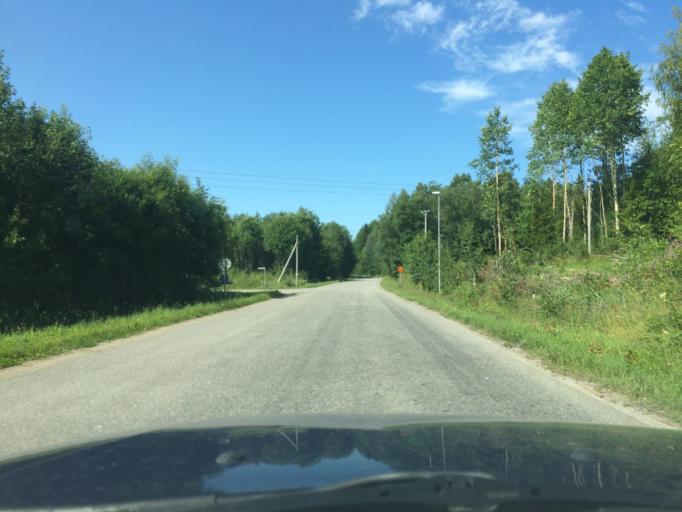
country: SE
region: Norrbotten
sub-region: Pitea Kommun
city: Norrfjarden
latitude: 65.3687
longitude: 21.4051
